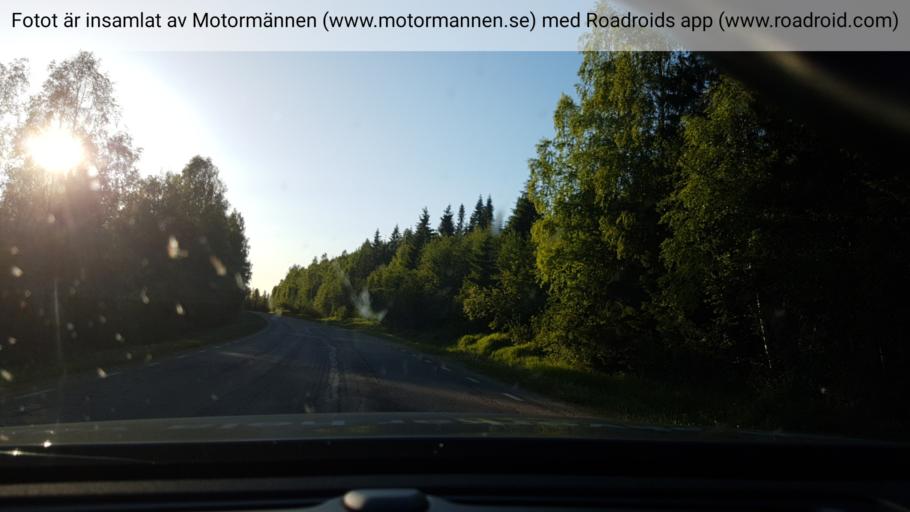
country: SE
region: Vaesterbotten
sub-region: Vannas Kommun
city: Vaennaes
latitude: 63.8600
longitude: 19.7465
